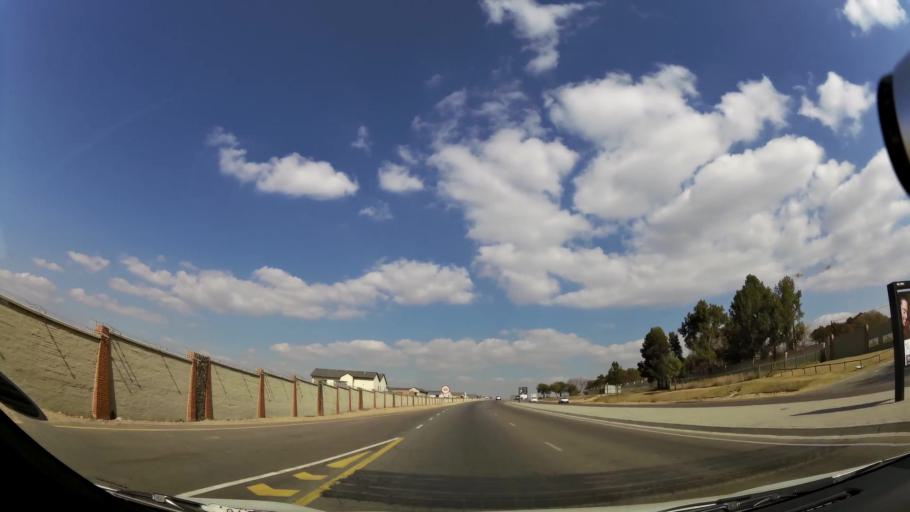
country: ZA
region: Gauteng
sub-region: City of Johannesburg Metropolitan Municipality
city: Midrand
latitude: -26.0288
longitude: 28.0911
